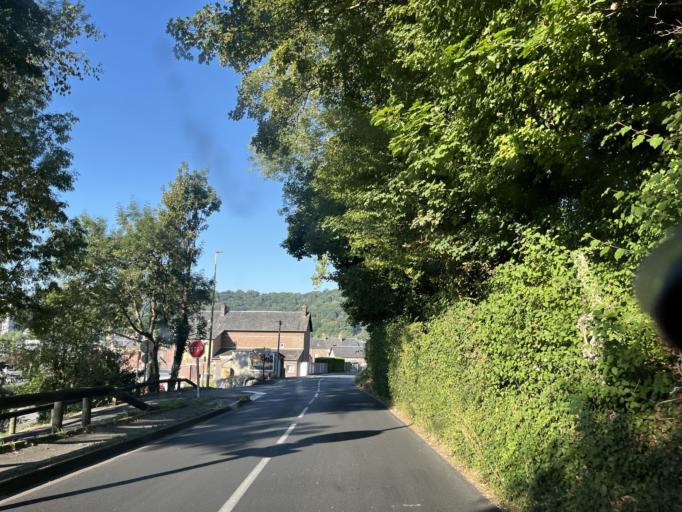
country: FR
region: Haute-Normandie
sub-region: Departement de la Seine-Maritime
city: Lillebonne
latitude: 49.5236
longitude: 0.5376
